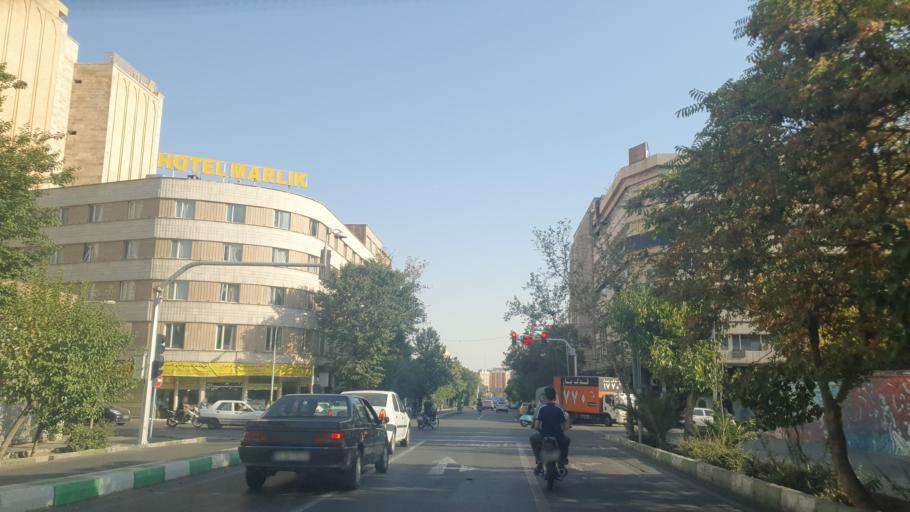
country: IR
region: Tehran
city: Tehran
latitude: 35.7062
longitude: 51.4258
